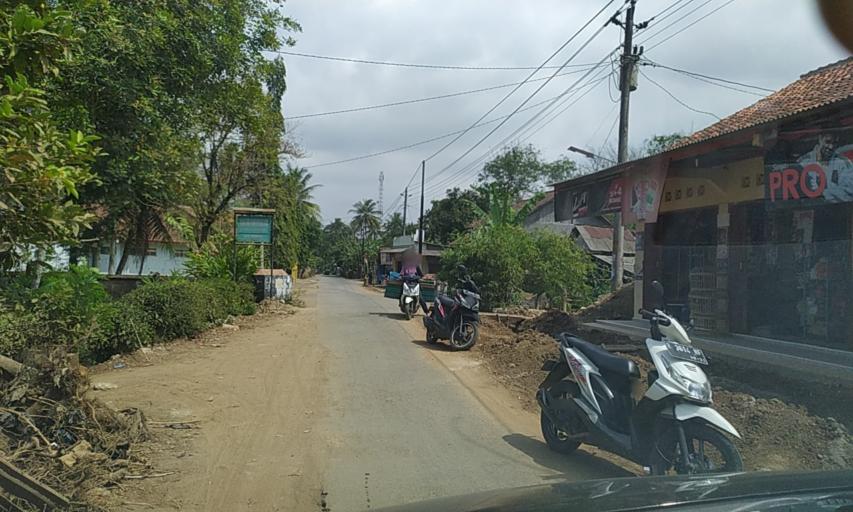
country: ID
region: Central Java
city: Sawoan
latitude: -7.6203
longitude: 109.0704
